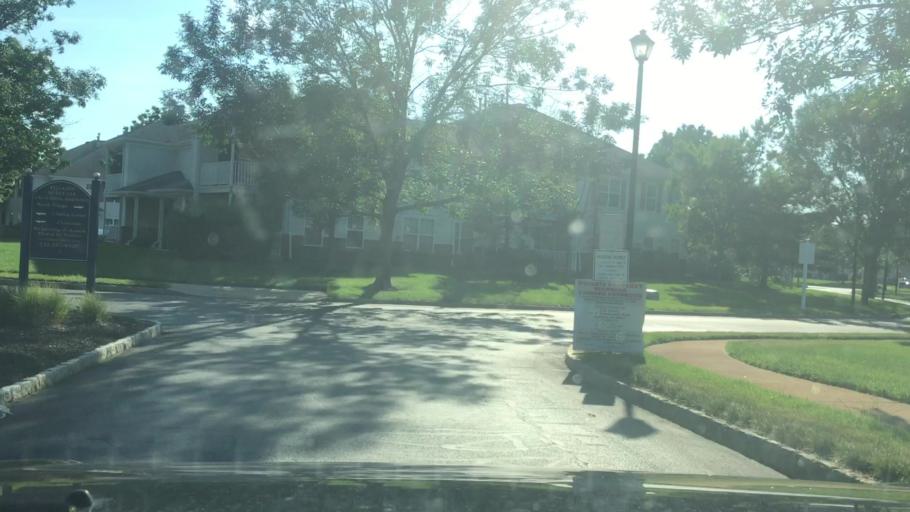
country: US
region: New Jersey
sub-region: Ocean County
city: Toms River
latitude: 39.9890
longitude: -74.1971
